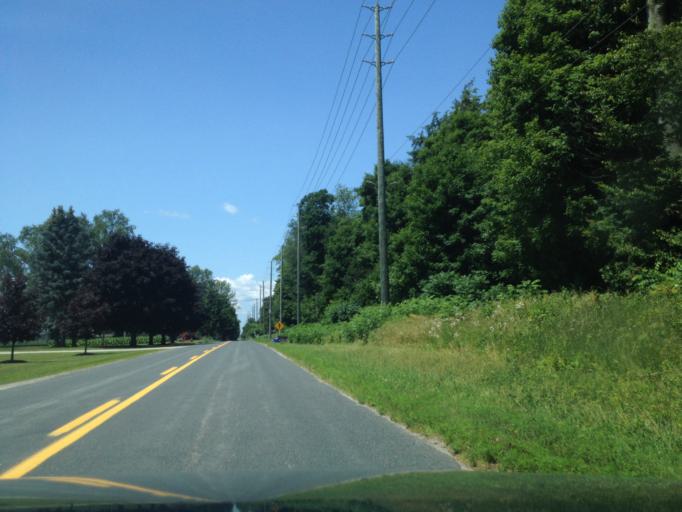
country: CA
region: Ontario
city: Aylmer
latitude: 42.6505
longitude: -80.7678
